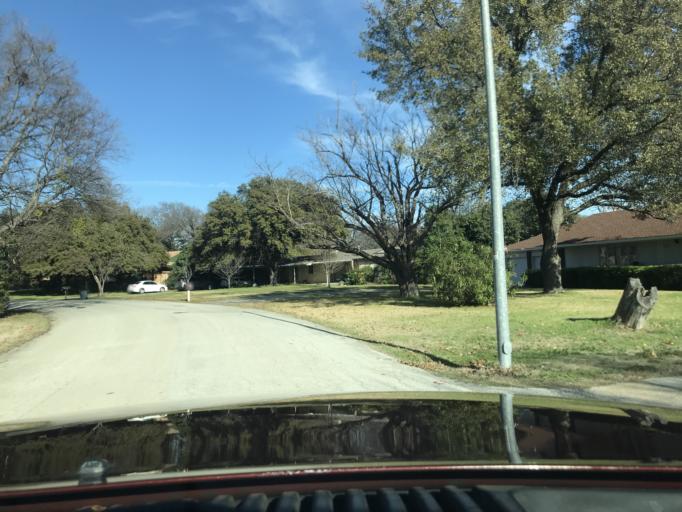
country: US
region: Texas
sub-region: Tarrant County
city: Edgecliff Village
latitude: 32.6592
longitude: -97.3435
